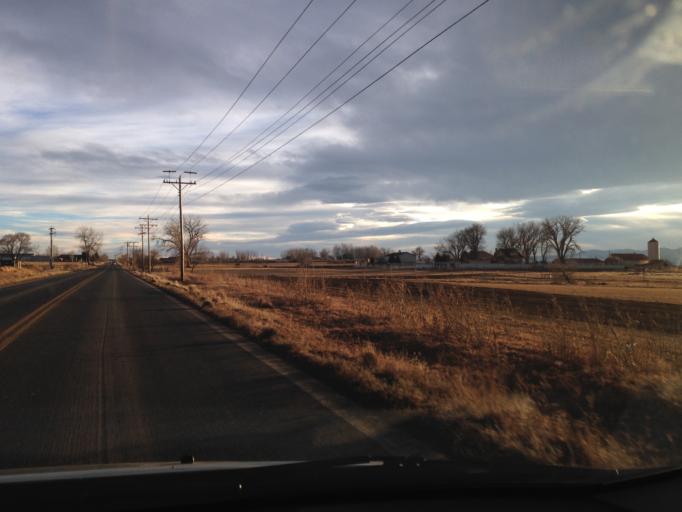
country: US
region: Colorado
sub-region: Weld County
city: Firestone
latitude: 40.1200
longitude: -104.9989
